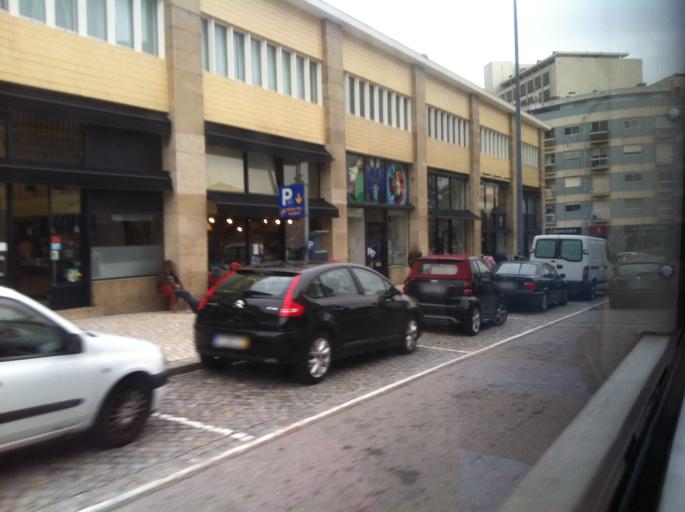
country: PT
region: Porto
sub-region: Porto
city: Porto
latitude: 41.1554
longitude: -8.6294
